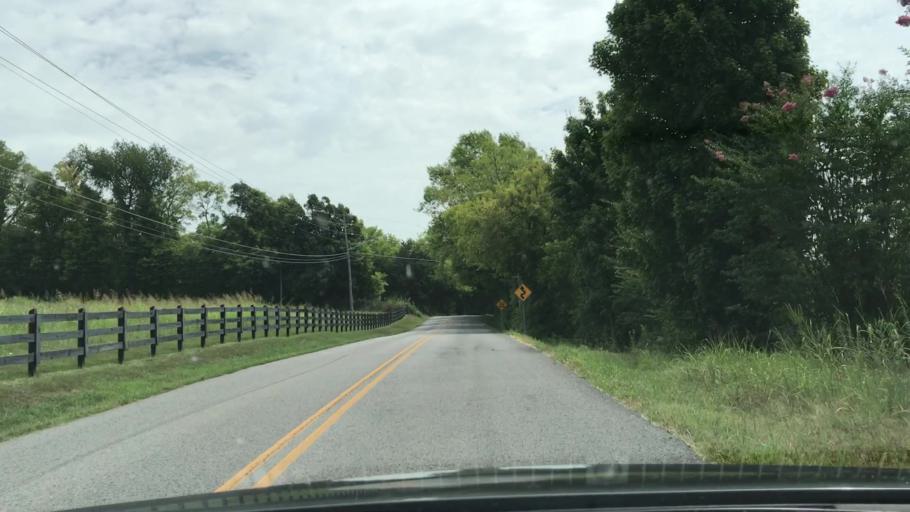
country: US
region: Tennessee
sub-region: Rutherford County
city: La Vergne
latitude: 35.9740
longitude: -86.5914
